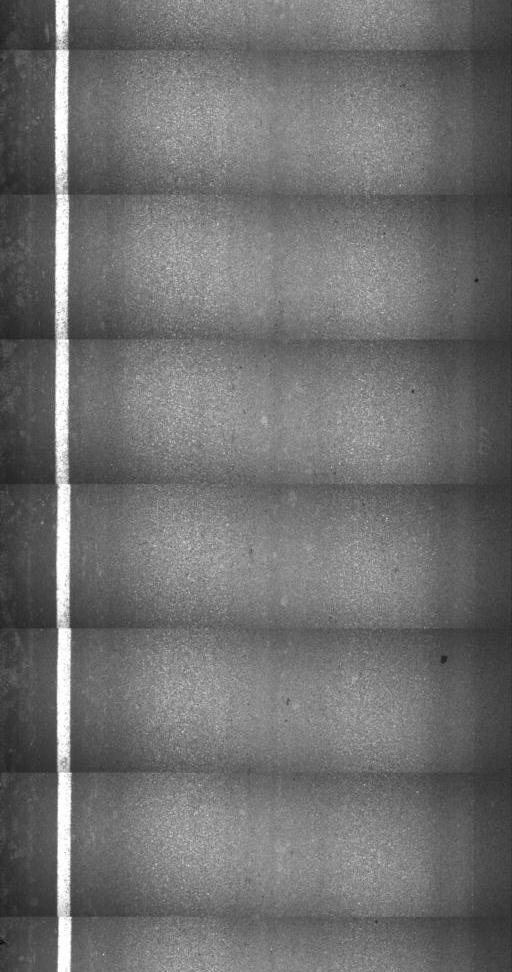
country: US
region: New Hampshire
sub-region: Grafton County
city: Woodsville
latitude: 44.1828
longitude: -72.0619
